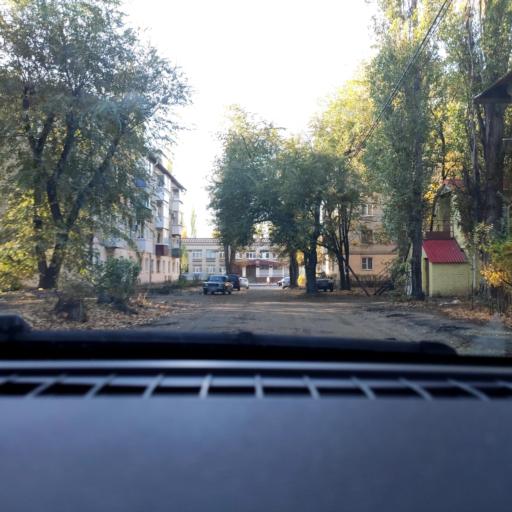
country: RU
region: Voronezj
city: Maslovka
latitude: 51.6144
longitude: 39.2527
